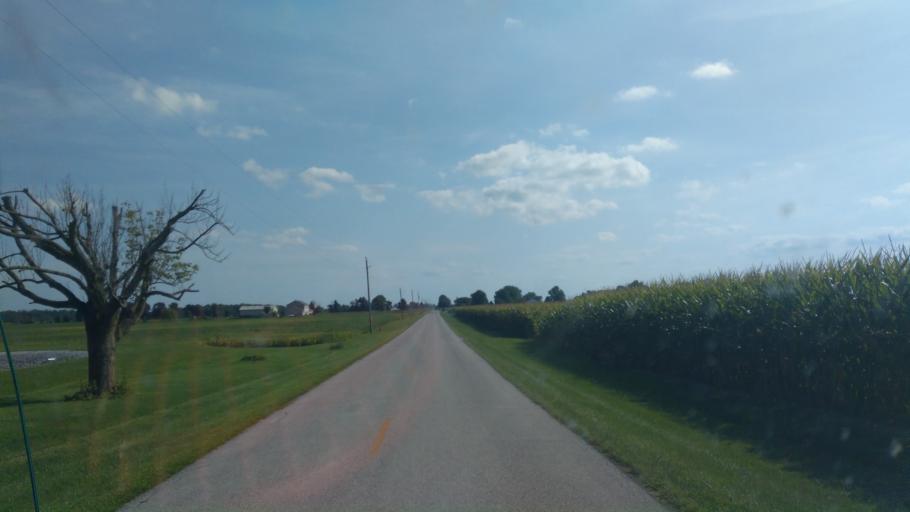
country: US
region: Ohio
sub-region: Hardin County
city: Forest
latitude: 40.7095
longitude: -83.5145
